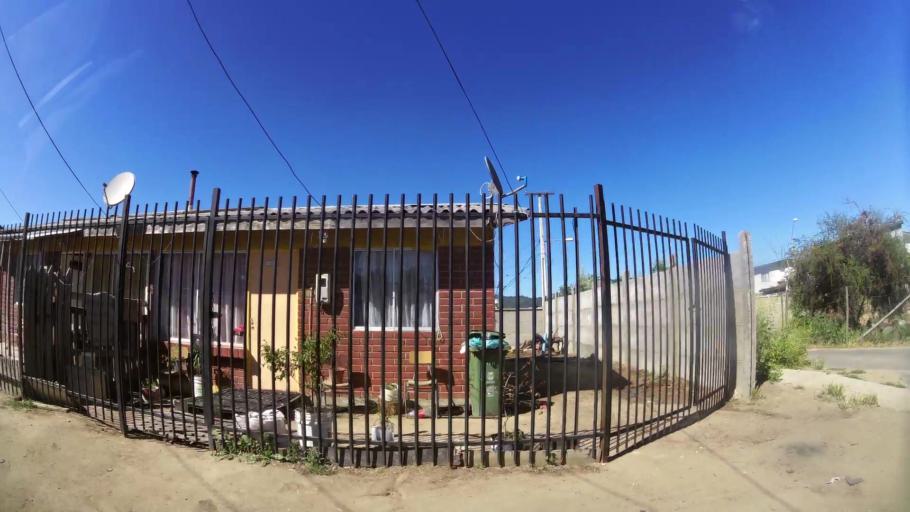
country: CL
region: Valparaiso
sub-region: Provincia de Marga Marga
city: Quilpue
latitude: -33.3214
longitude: -71.3969
